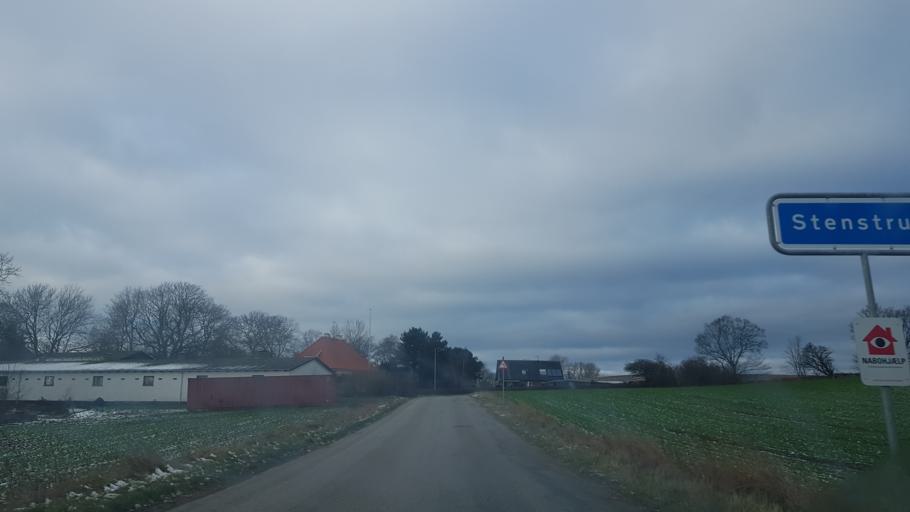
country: DK
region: Zealand
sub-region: Odsherred Kommune
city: Hojby
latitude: 55.9266
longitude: 11.5576
